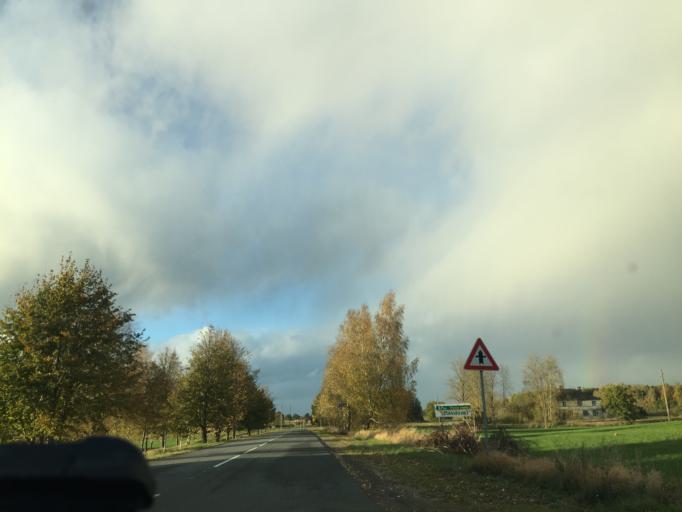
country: LV
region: Broceni
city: Broceni
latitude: 56.8601
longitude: 22.3819
